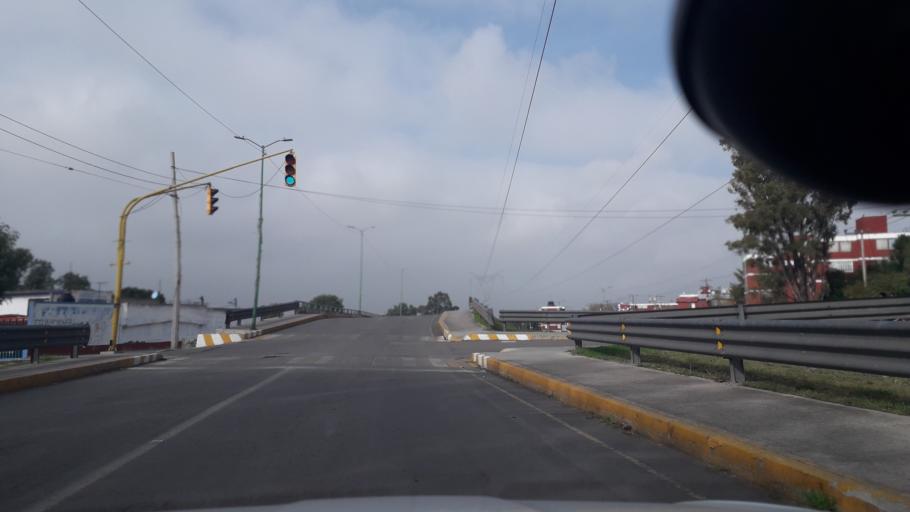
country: MX
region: Mexico
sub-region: Jaltenco
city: Alborada Jaltenco
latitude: 19.6447
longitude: -99.0803
